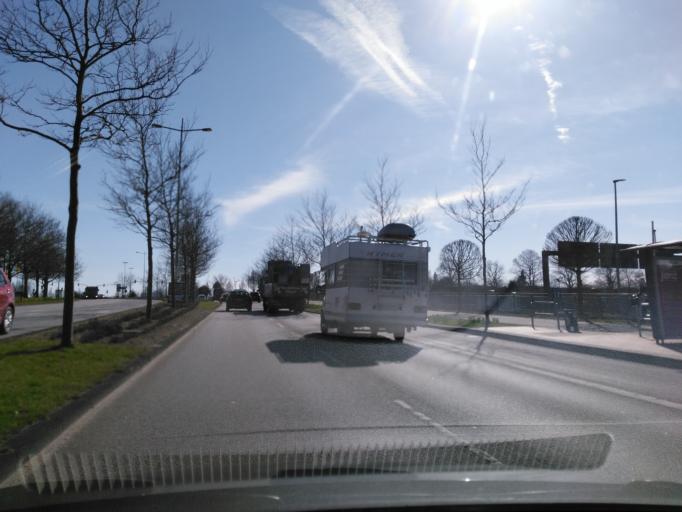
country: DE
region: Schleswig-Holstein
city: Kiel
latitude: 54.3135
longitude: 10.1093
